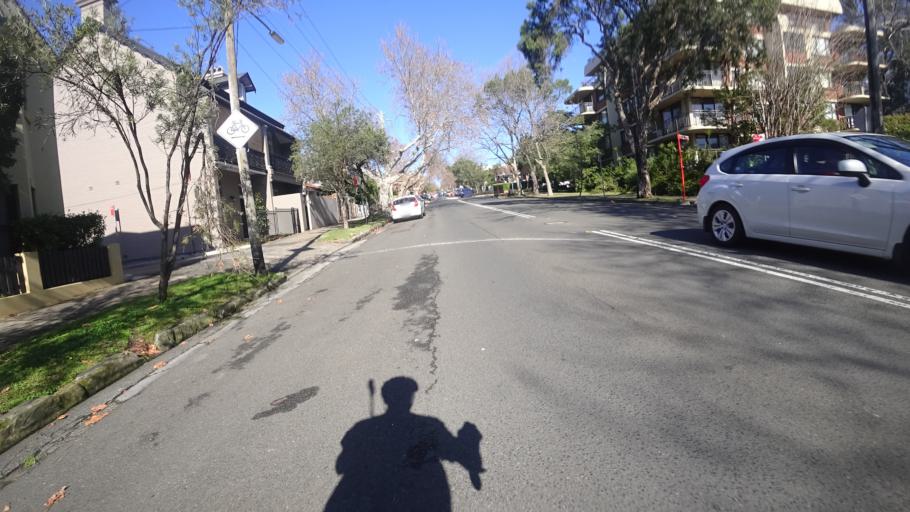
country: AU
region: New South Wales
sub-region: North Sydney
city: Crows Nest
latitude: -33.8227
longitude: 151.2031
